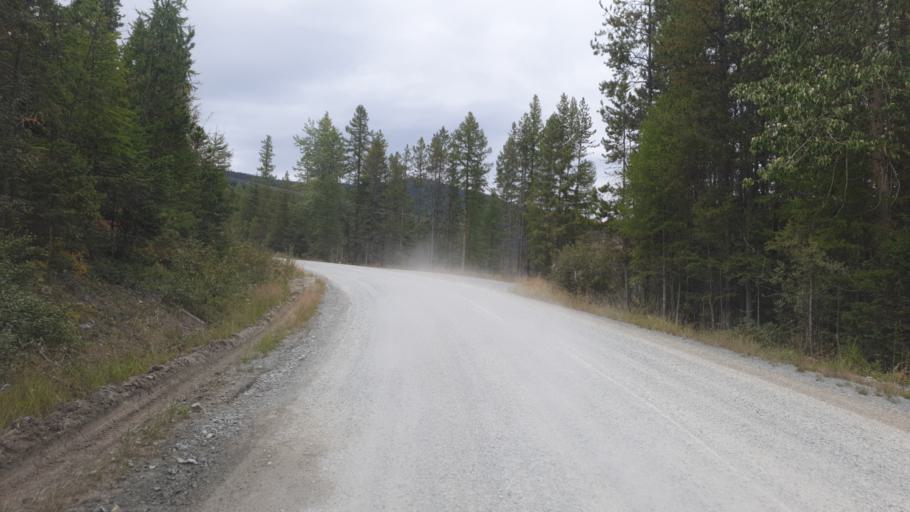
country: US
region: Montana
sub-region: Flathead County
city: Lakeside
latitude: 47.9936
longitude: -114.3205
